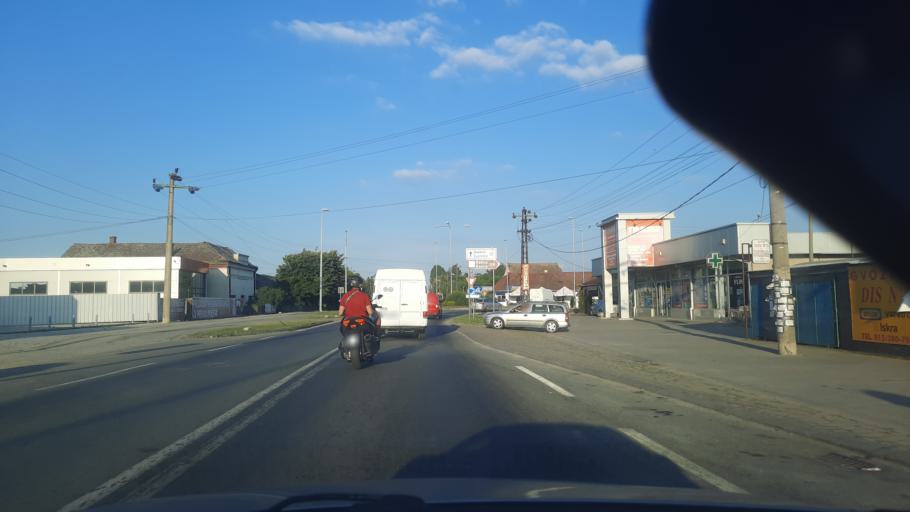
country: RS
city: Jelenca
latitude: 44.7386
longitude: 19.7329
